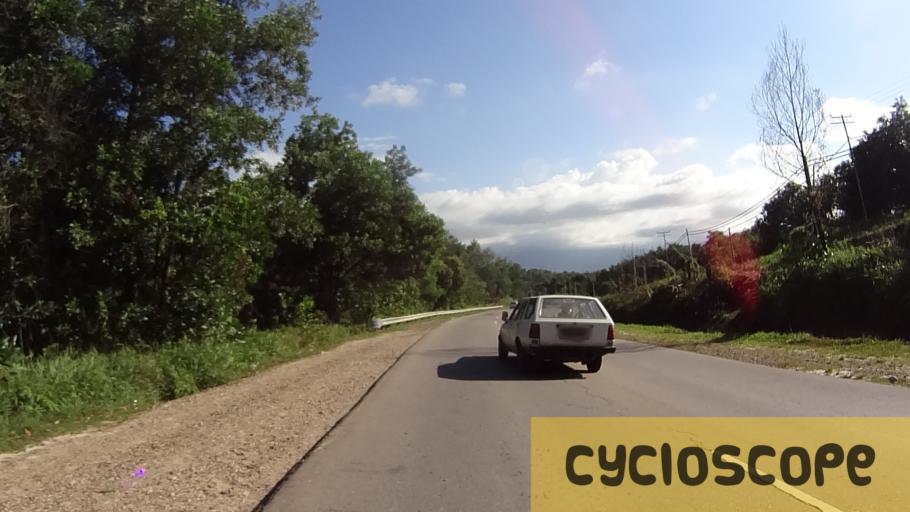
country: MY
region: Sabah
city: Bandar Labuan
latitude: 5.0135
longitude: 115.5380
